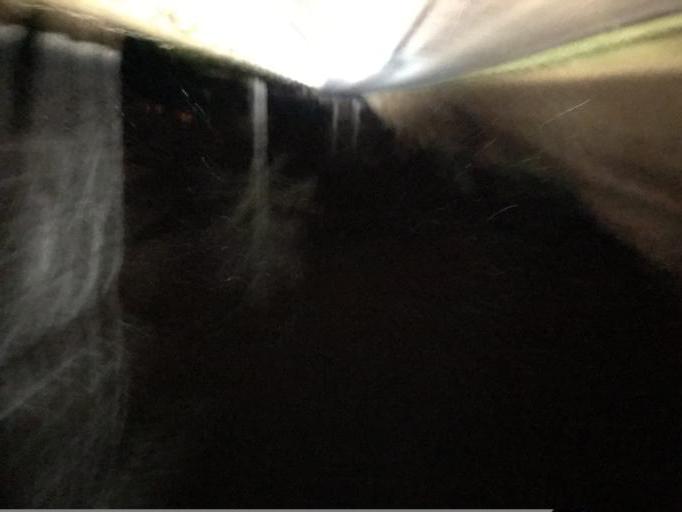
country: FR
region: Auvergne
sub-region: Departement du Puy-de-Dome
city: Saint-Remy-sur-Durolle
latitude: 45.9023
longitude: 3.6309
